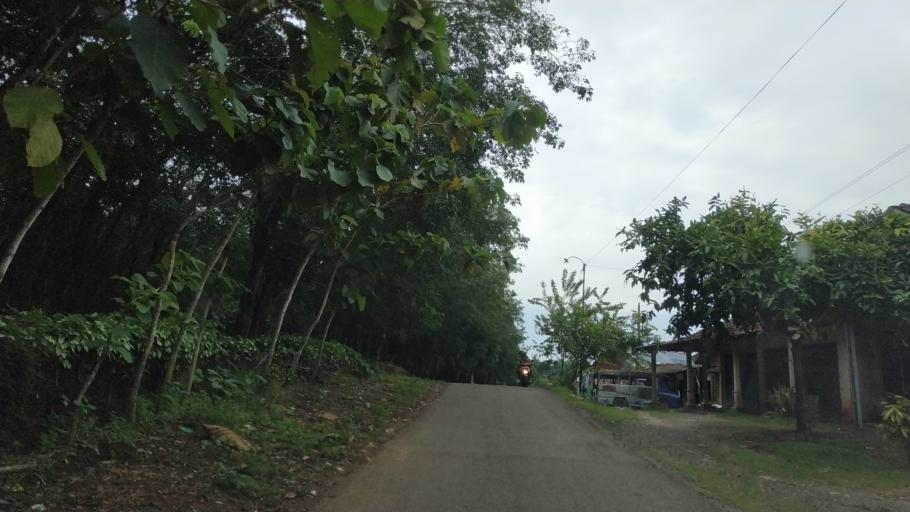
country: ID
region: Central Java
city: Krajan Tegalombo
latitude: -6.4338
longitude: 110.9824
